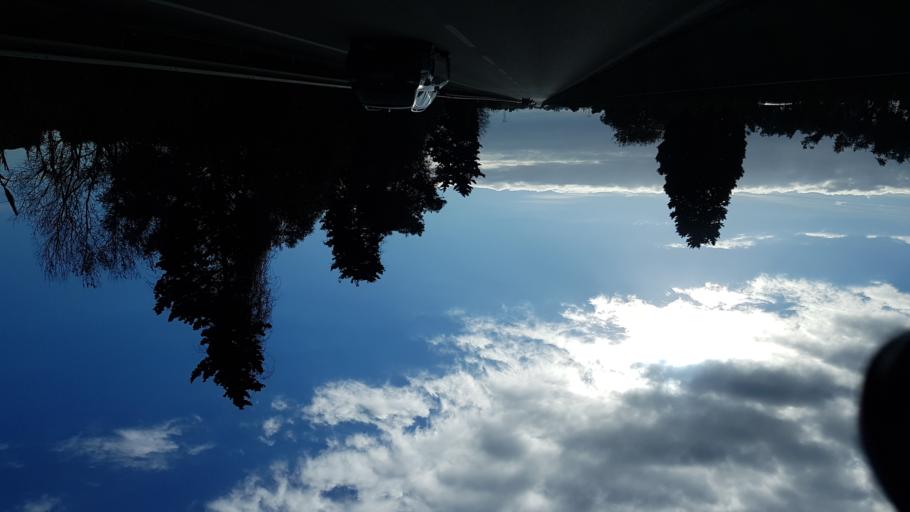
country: IT
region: Apulia
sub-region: Provincia di Brindisi
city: La Rosa
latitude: 40.5757
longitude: 17.9810
